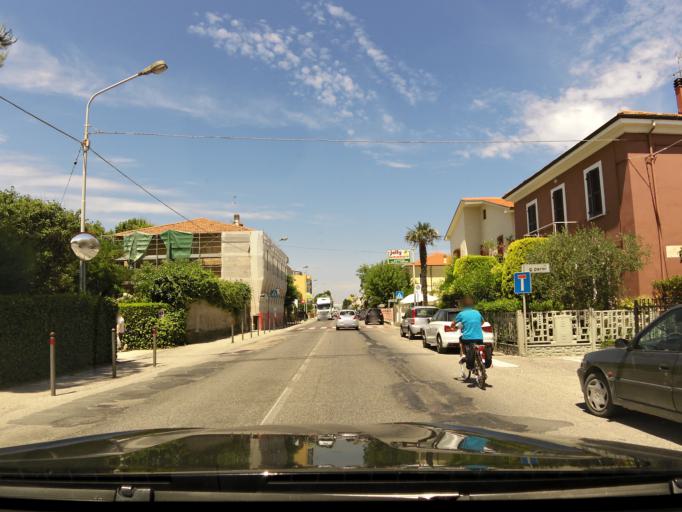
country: IT
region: The Marches
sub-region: Provincia di Ancona
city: Senigallia
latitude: 43.7231
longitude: 13.2095
